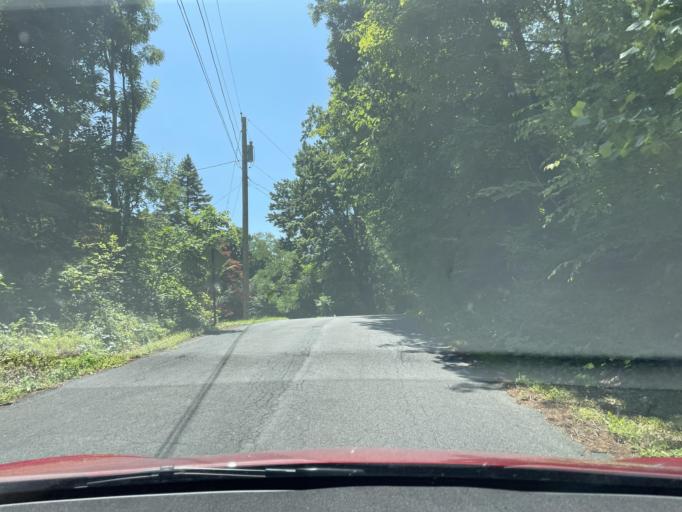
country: US
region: New York
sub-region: Ulster County
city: Lake Katrine
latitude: 42.0174
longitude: -73.9763
